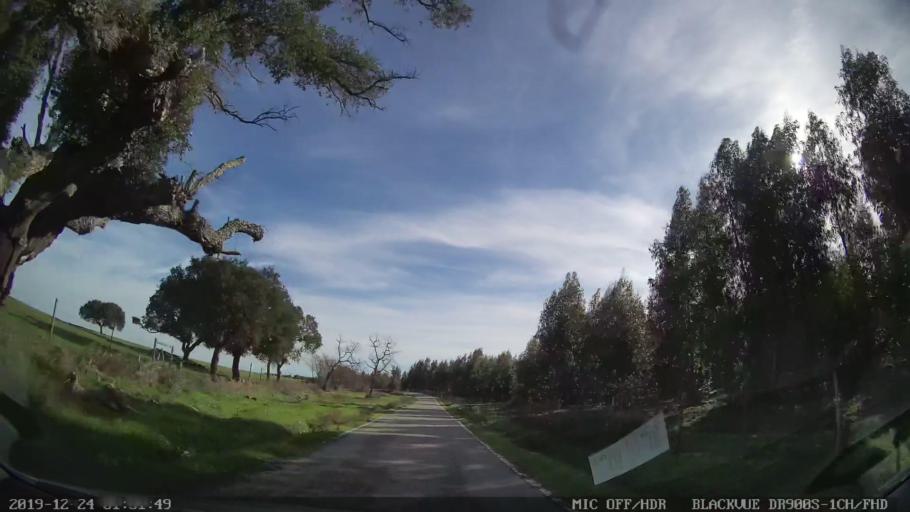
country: PT
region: Portalegre
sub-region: Nisa
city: Nisa
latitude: 39.4947
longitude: -7.7533
